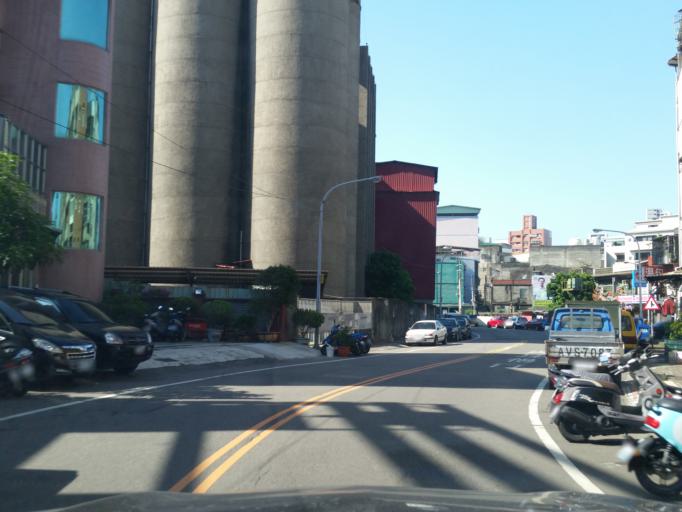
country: TW
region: Taiwan
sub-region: Taoyuan
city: Taoyuan
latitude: 24.9883
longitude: 121.3193
